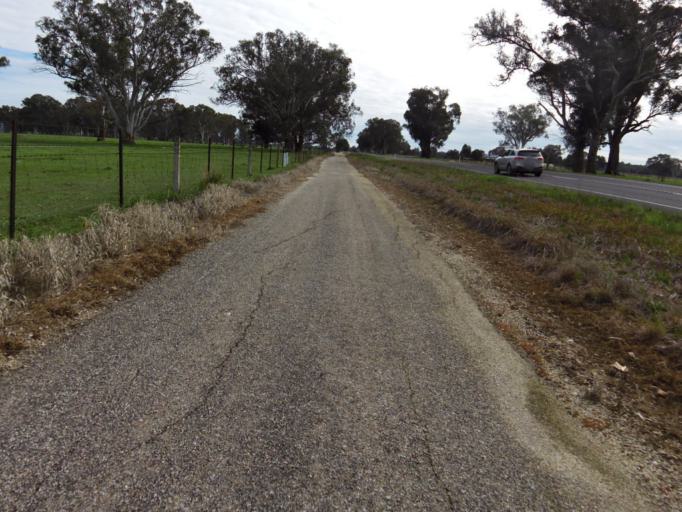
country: AU
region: Victoria
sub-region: Wangaratta
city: Wangaratta
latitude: -36.4225
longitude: 146.3579
